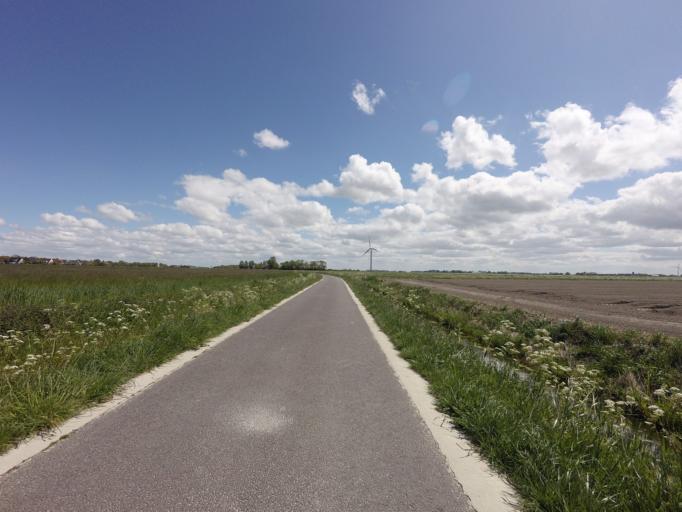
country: NL
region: Friesland
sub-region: Gemeente Harlingen
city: Harlingen
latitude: 53.1378
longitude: 5.4273
